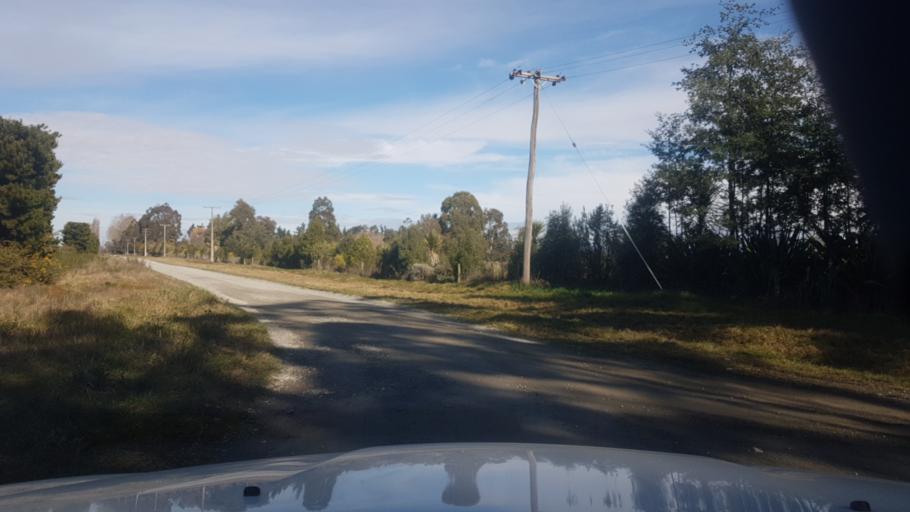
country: NZ
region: Canterbury
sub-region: Timaru District
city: Pleasant Point
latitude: -44.1446
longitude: 171.2816
